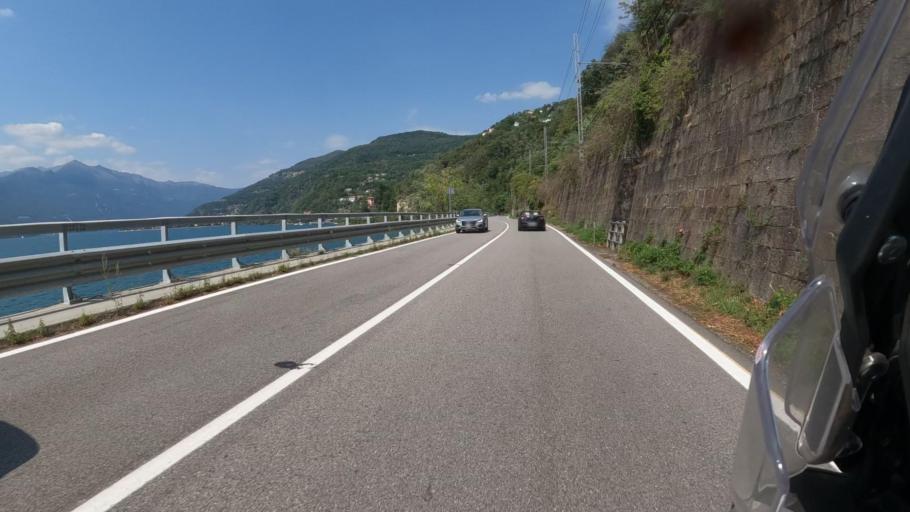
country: IT
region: Lombardy
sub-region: Provincia di Varese
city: Luino
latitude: 46.0145
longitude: 8.7508
